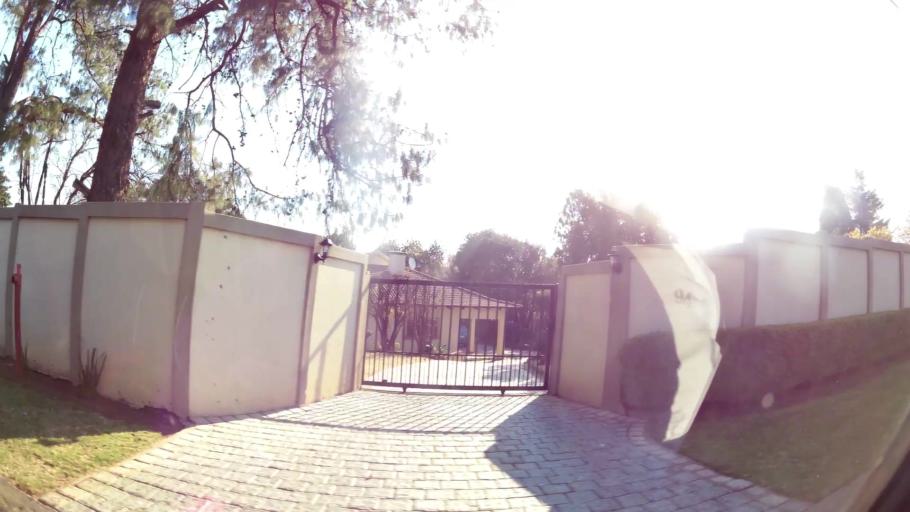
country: ZA
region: Gauteng
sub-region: City of Johannesburg Metropolitan Municipality
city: Roodepoort
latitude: -26.0999
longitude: 27.9682
